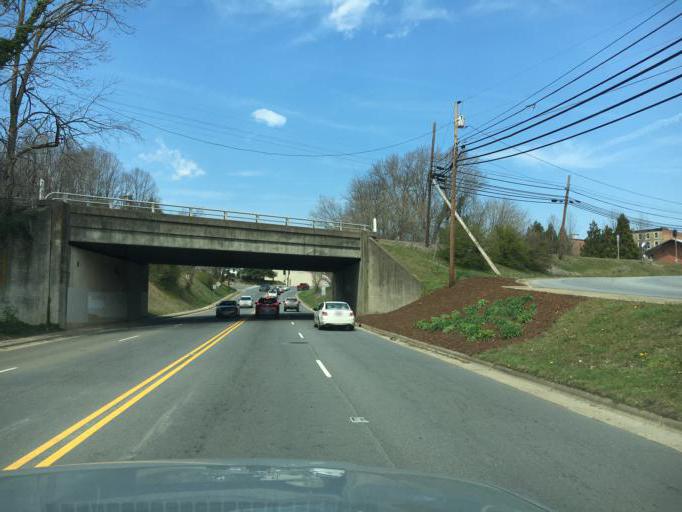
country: US
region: North Carolina
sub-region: McDowell County
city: Marion
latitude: 35.6800
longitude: -82.0116
